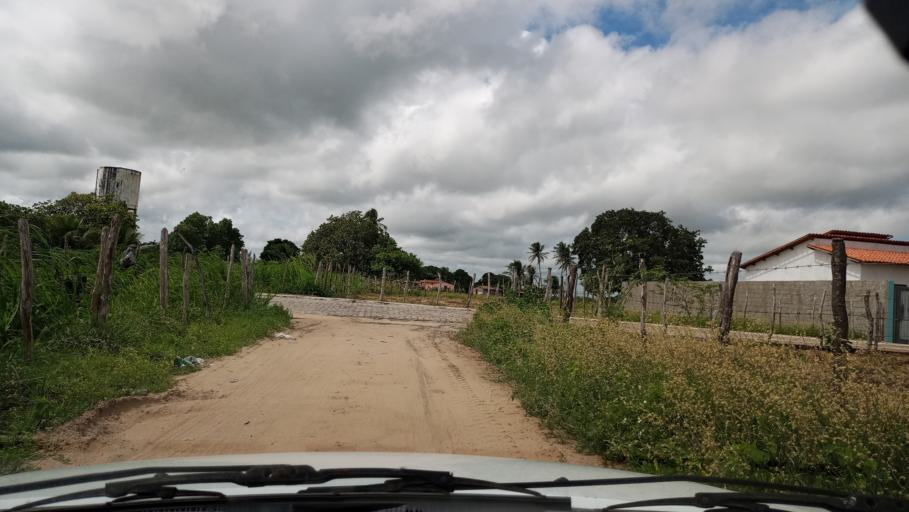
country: BR
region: Rio Grande do Norte
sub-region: Brejinho
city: Brejinho
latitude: -6.1551
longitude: -35.4364
